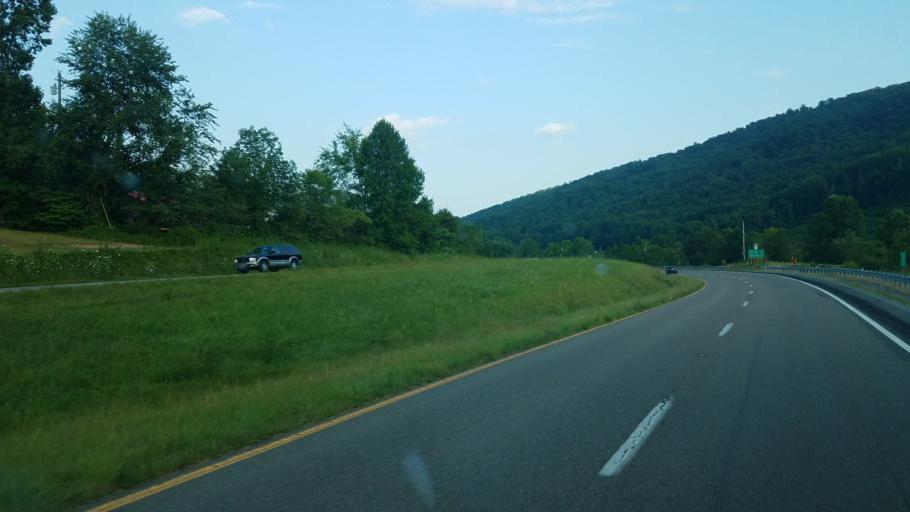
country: US
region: Virginia
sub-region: Lee County
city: Dryden
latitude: 36.7640
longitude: -82.8219
